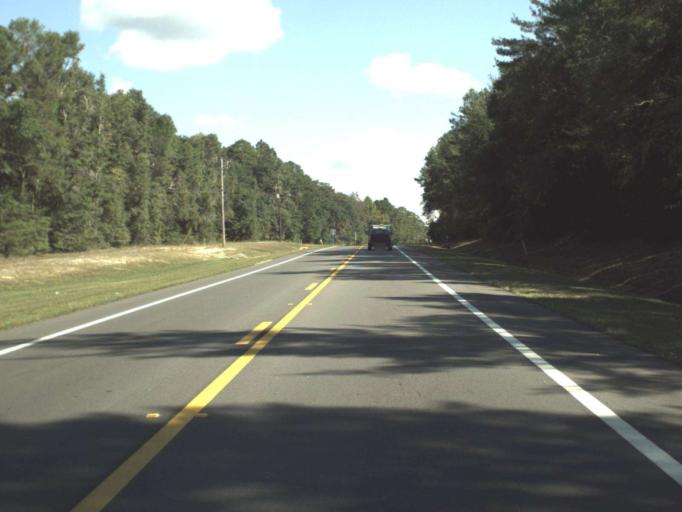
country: US
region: Florida
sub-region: Walton County
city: Freeport
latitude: 30.5011
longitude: -86.1436
